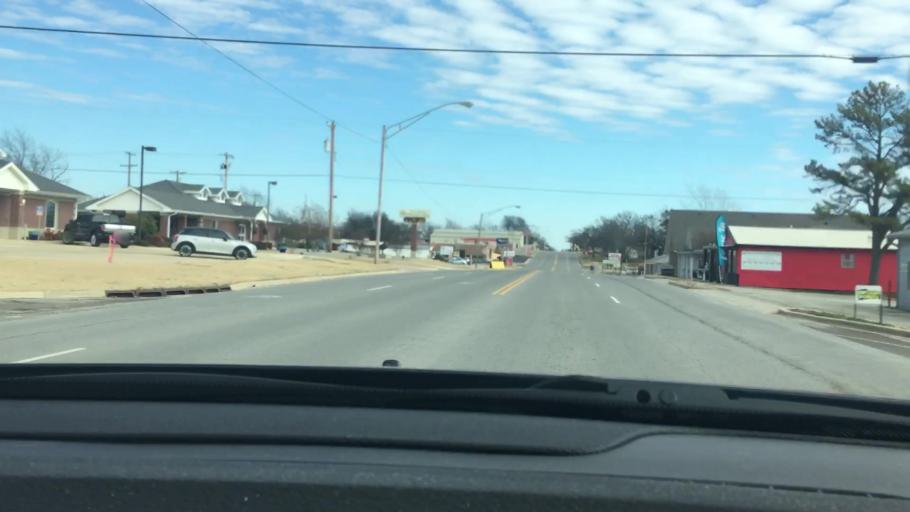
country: US
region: Oklahoma
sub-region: Garvin County
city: Stratford
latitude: 34.7966
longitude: -96.9661
